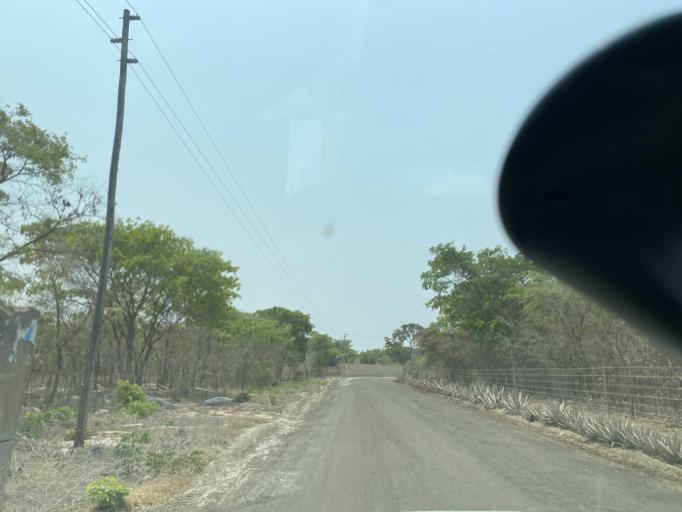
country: ZM
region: Lusaka
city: Lusaka
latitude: -15.5110
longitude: 28.4441
